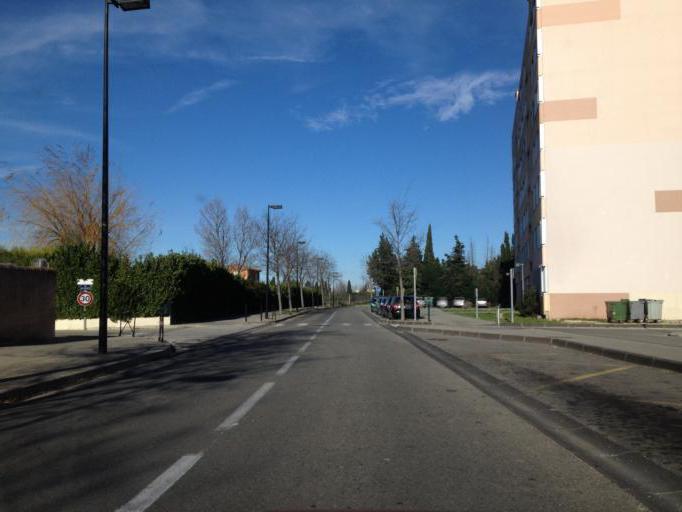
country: FR
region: Provence-Alpes-Cote d'Azur
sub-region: Departement du Vaucluse
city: Orange
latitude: 44.1547
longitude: 4.7992
